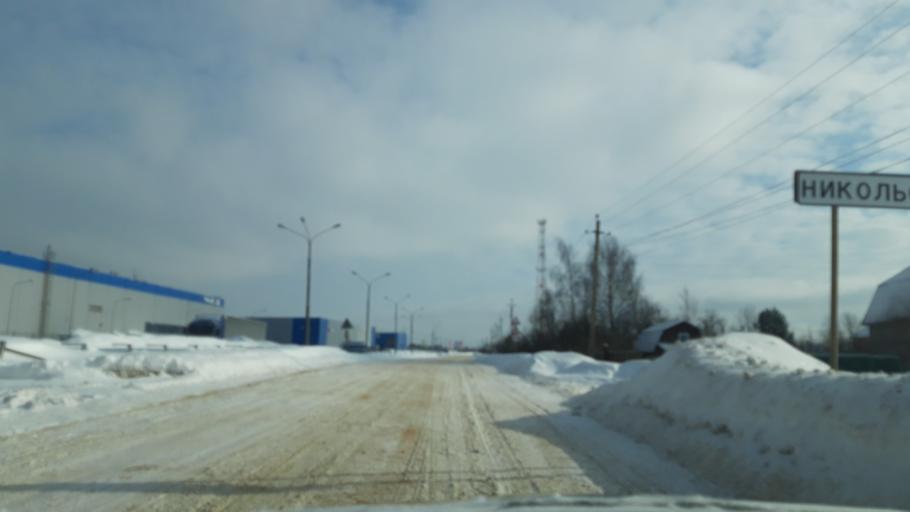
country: RU
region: Moskovskaya
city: Yermolino
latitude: 56.1445
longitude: 37.3743
